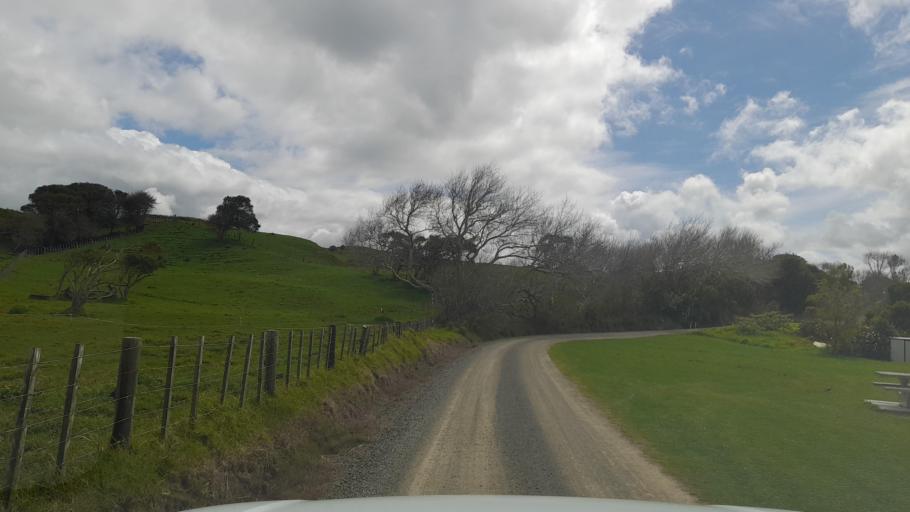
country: NZ
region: Auckland
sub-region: Auckland
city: Wellsford
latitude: -36.2212
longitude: 174.3205
